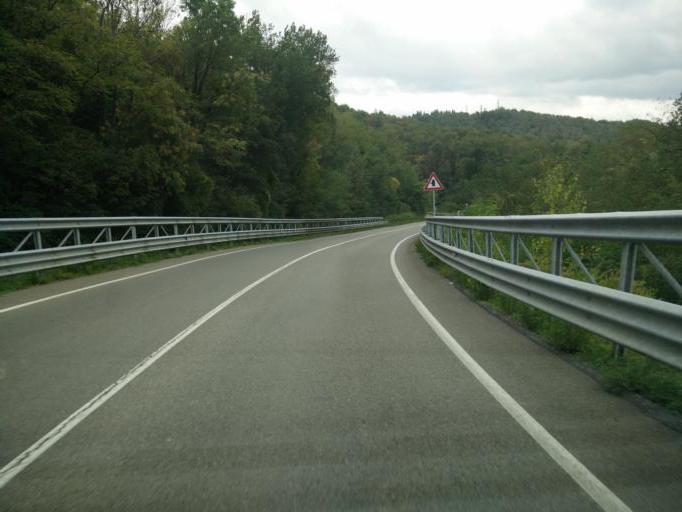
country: IT
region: Tuscany
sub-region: Provincia di Massa-Carrara
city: Fivizzano
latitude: 44.2267
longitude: 10.1172
